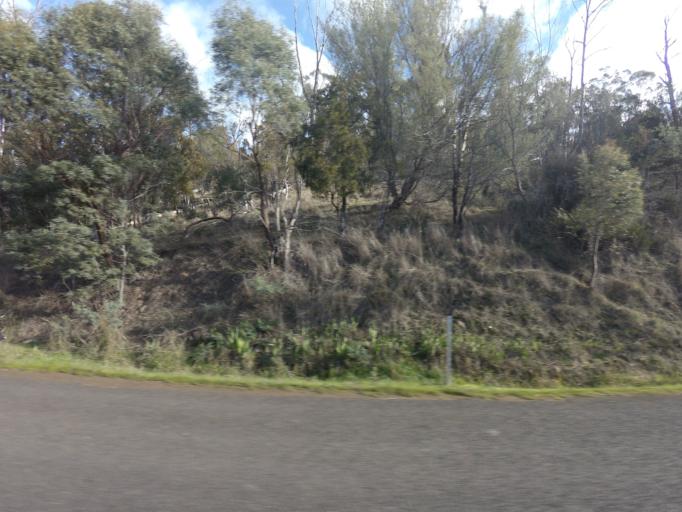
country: AU
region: Tasmania
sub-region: Derwent Valley
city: New Norfolk
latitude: -42.8033
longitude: 147.1376
